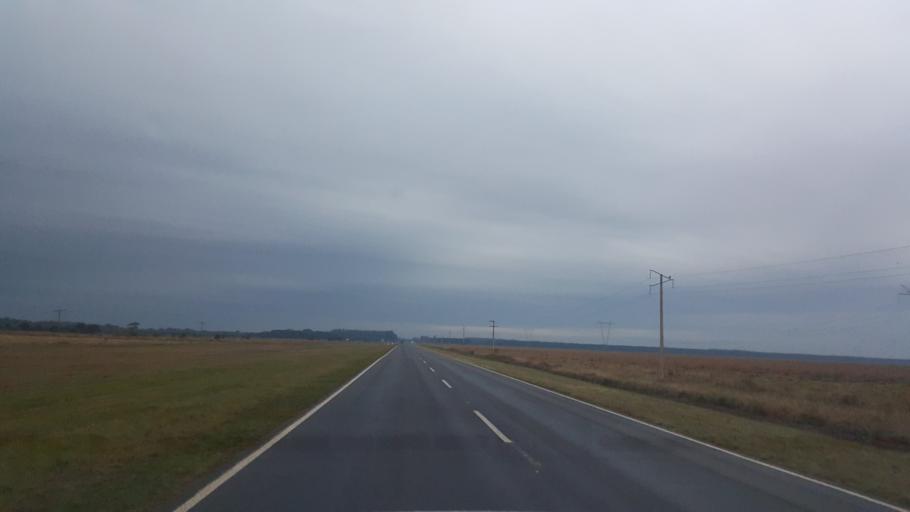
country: AR
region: Corrientes
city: Ituzaingo
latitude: -27.5988
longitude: -56.4604
